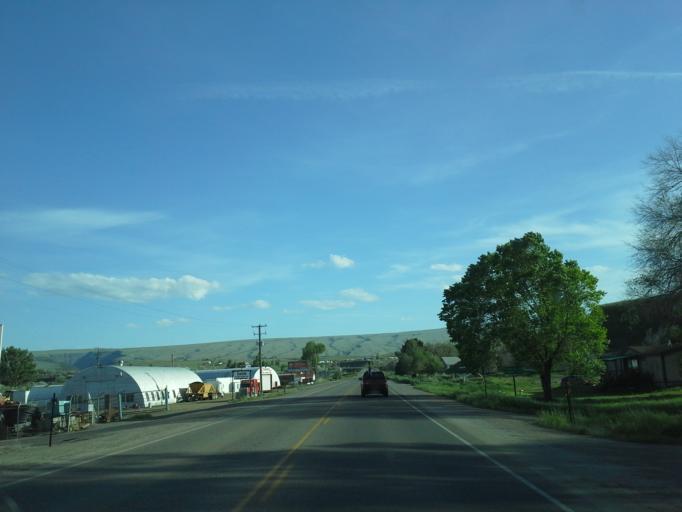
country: US
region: Wyoming
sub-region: Hot Springs County
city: Thermopolis
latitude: 43.6268
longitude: -108.2198
